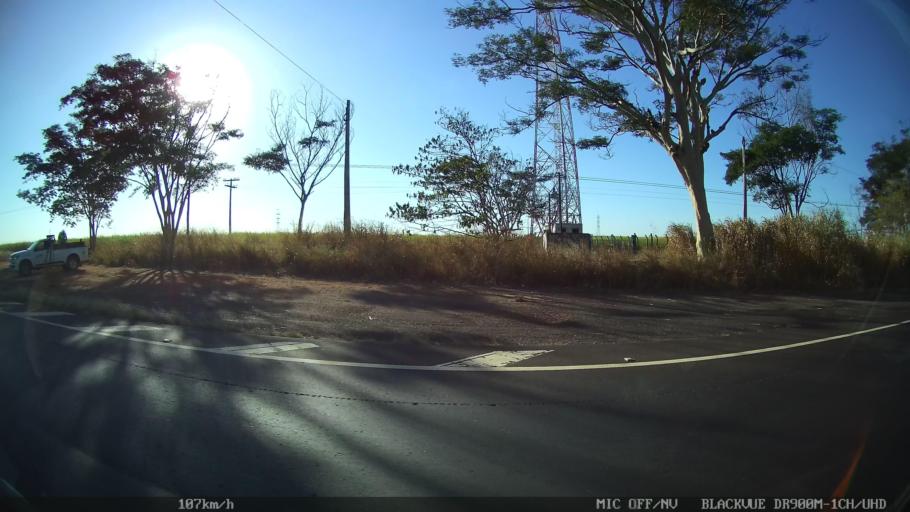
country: BR
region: Sao Paulo
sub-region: Guapiacu
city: Guapiacu
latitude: -20.7353
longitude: -49.0747
